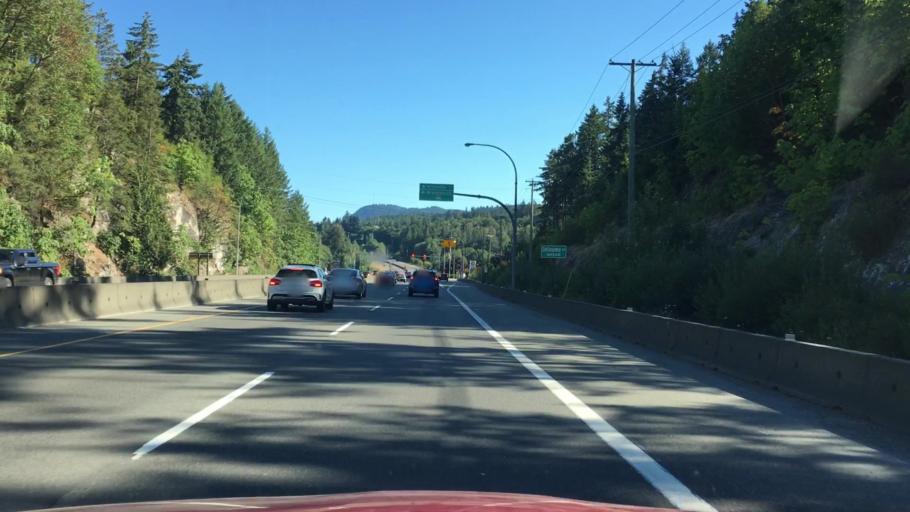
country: CA
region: British Columbia
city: North Saanich
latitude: 48.6549
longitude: -123.5607
